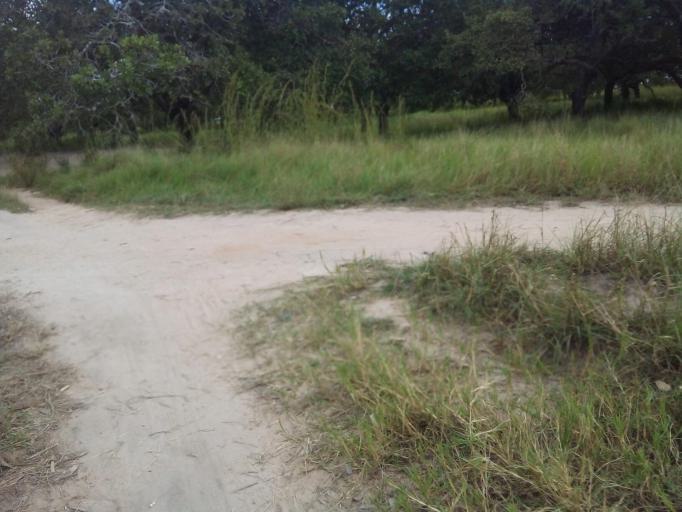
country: MZ
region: Zambezia
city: Quelimane
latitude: -17.5515
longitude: 36.7054
